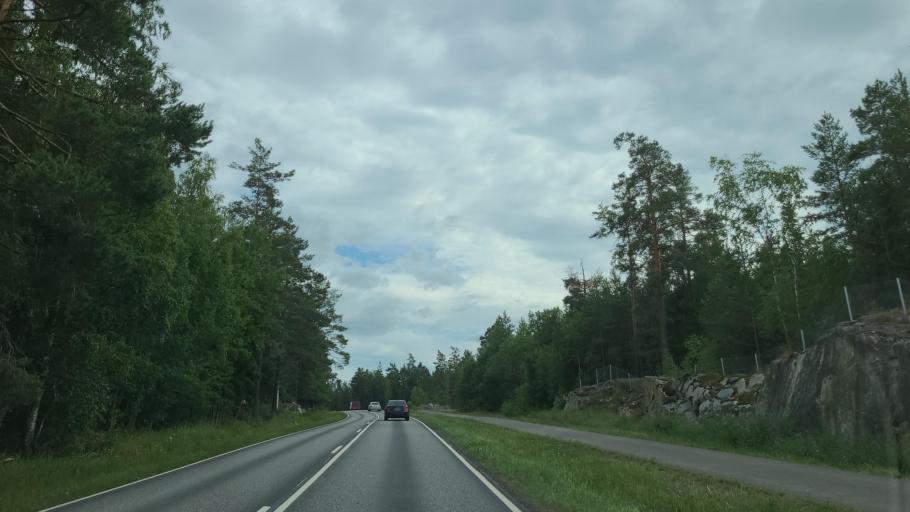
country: FI
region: Varsinais-Suomi
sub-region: Turku
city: Rymaettylae
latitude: 60.3975
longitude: 21.8993
